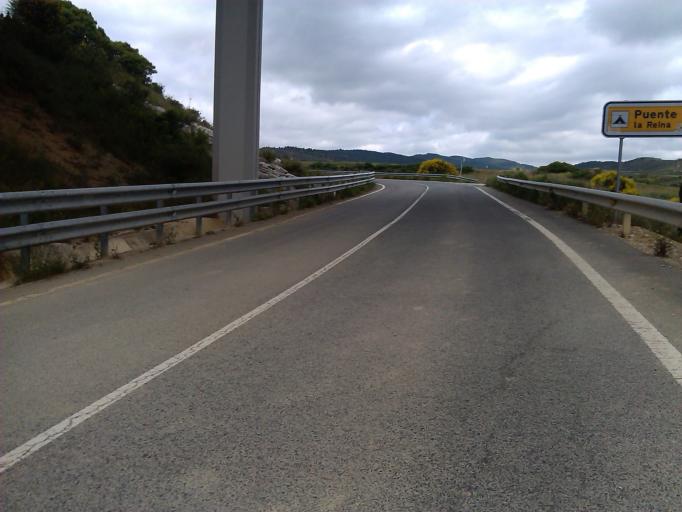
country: ES
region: Navarre
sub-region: Provincia de Navarra
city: Puente la Reina
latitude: 42.6701
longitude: -1.8289
